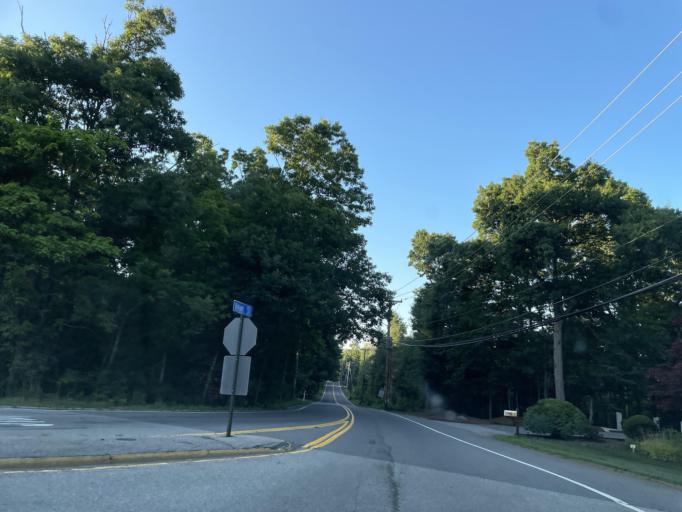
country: US
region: Massachusetts
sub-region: Plymouth County
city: Halifax
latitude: 42.0341
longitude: -70.8448
